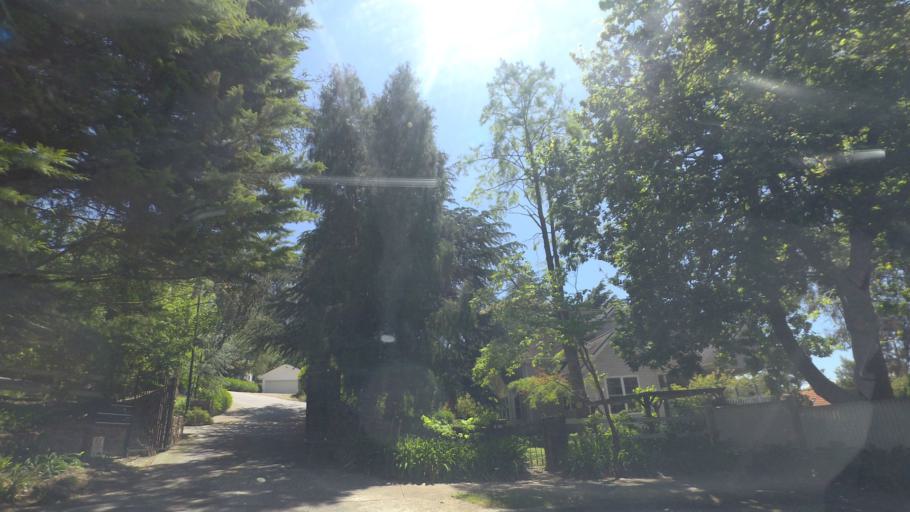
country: AU
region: Victoria
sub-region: Maroondah
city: Croydon Hills
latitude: -37.7775
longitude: 145.2811
